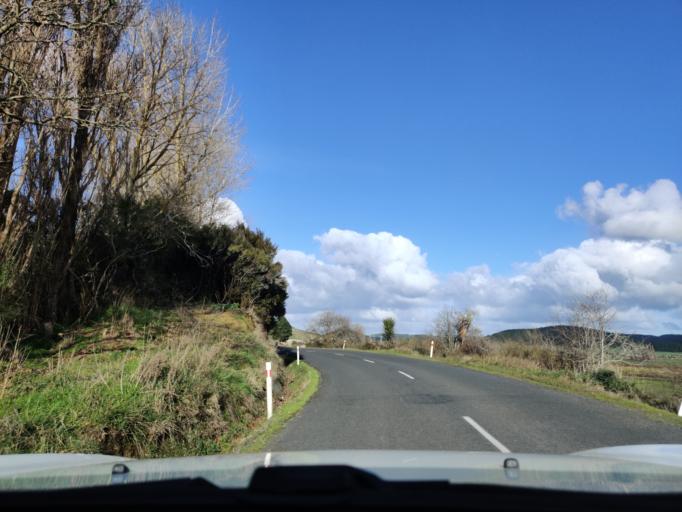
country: NZ
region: Waikato
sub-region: Waikato District
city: Te Kauwhata
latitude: -37.2705
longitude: 175.1984
